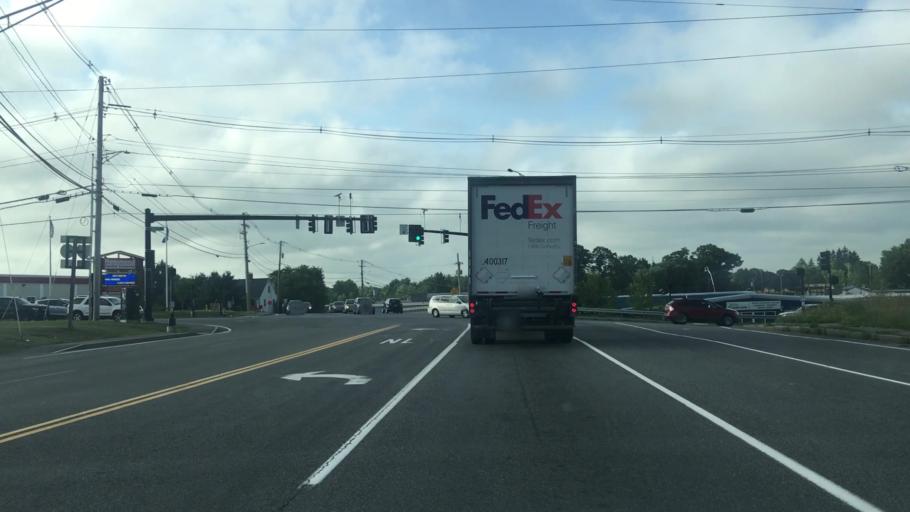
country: US
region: Maine
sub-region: Cumberland County
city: Westbrook
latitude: 43.6856
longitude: -70.3280
